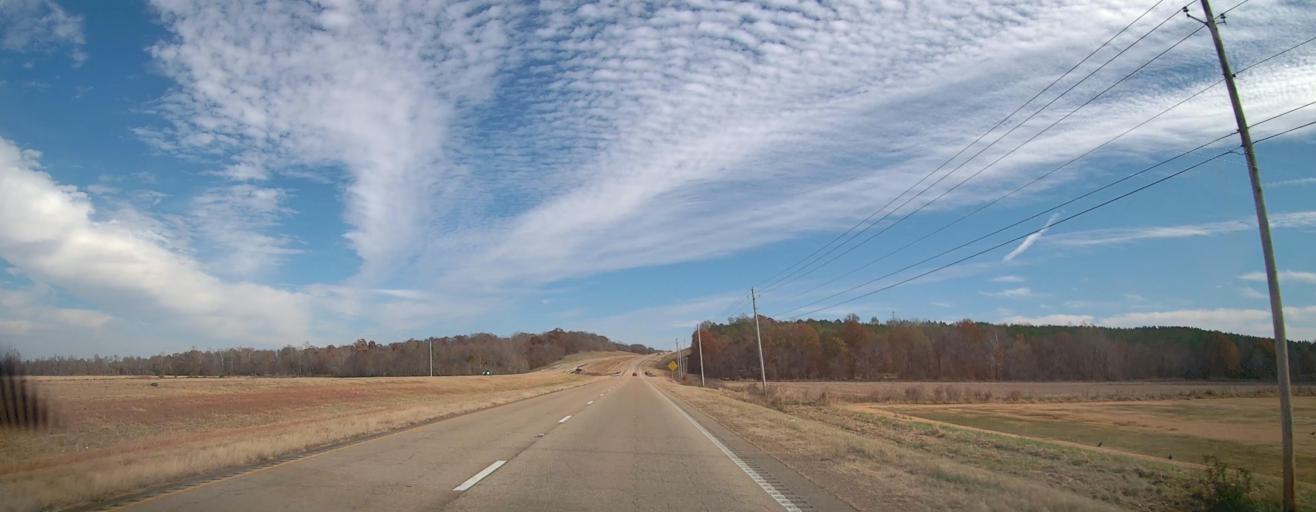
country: US
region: Mississippi
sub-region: Alcorn County
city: Corinth
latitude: 34.9320
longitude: -88.6565
